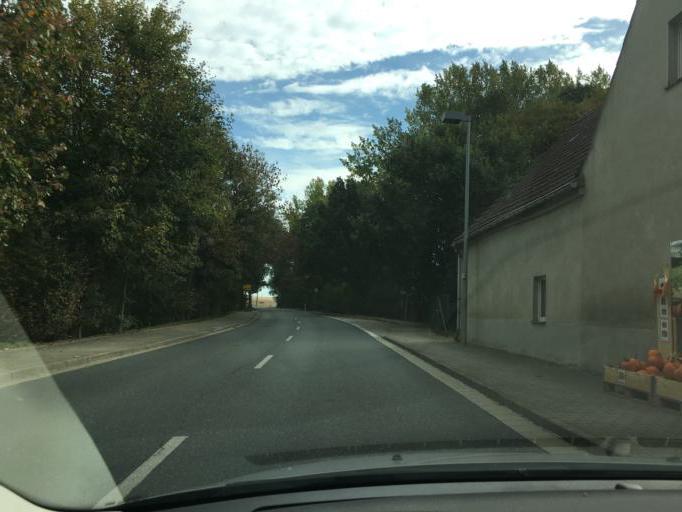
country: DE
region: Saxony
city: Lommatzsch
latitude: 51.2298
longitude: 13.3336
